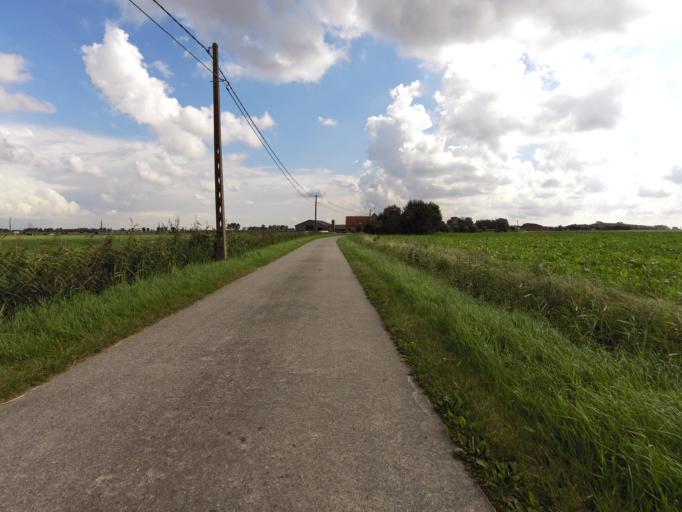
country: BE
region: Flanders
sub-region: Provincie West-Vlaanderen
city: Middelkerke
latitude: 51.1462
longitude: 2.8808
